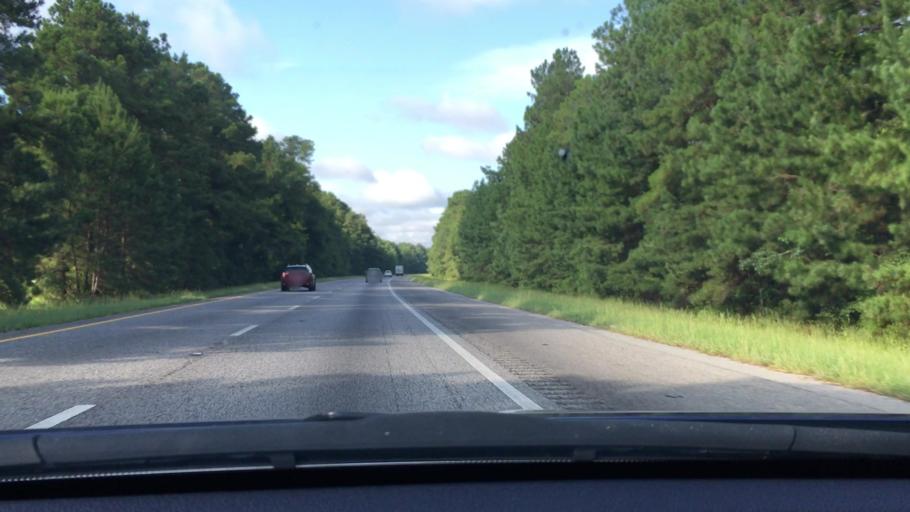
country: US
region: South Carolina
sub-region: Clarendon County
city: Manning
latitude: 33.6824
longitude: -80.2610
